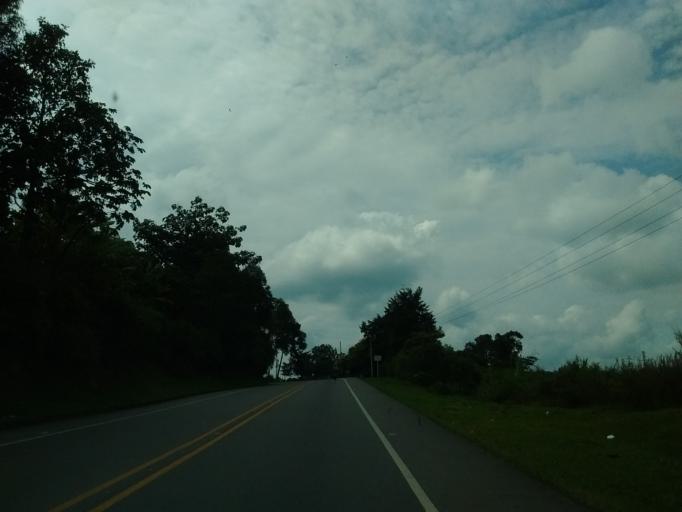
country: CO
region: Cauca
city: Morales
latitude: 2.7108
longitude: -76.5391
